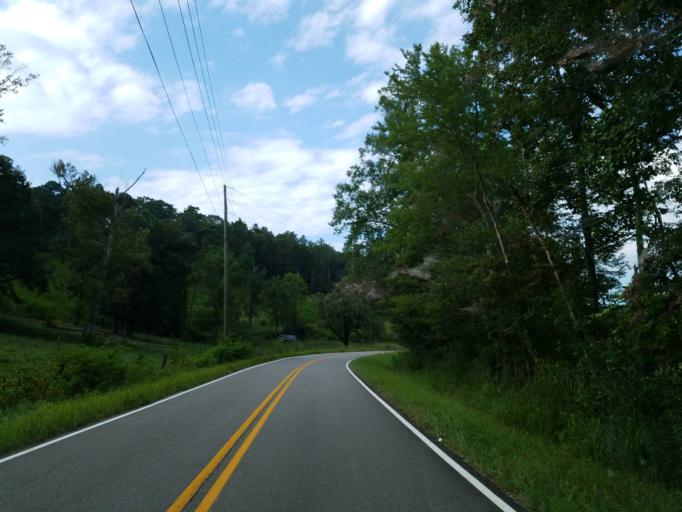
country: US
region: Georgia
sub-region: Gilmer County
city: Ellijay
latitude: 34.7668
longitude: -84.4214
